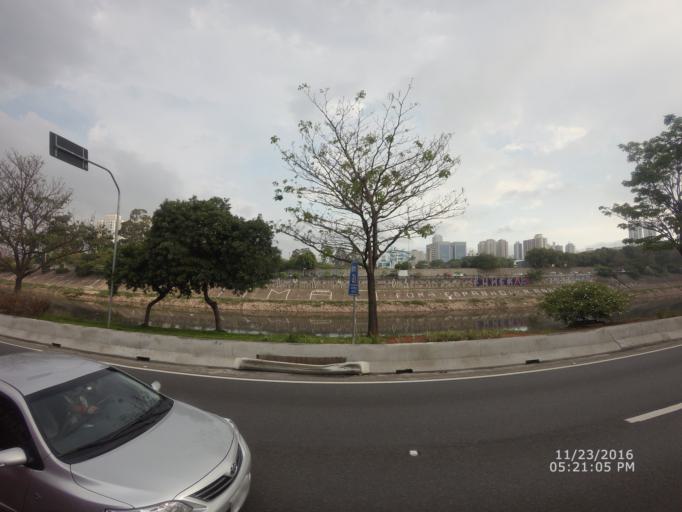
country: BR
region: Sao Paulo
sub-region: Guarulhos
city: Guarulhos
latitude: -23.5228
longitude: -46.5644
